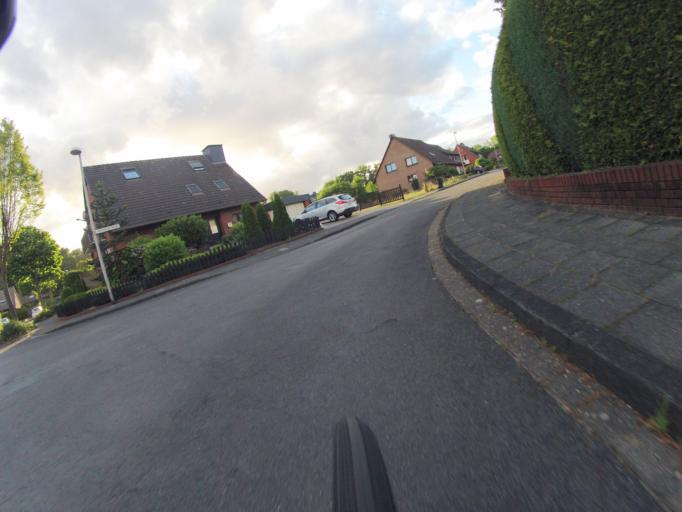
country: DE
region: North Rhine-Westphalia
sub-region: Regierungsbezirk Munster
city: Birgte
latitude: 52.2957
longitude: 7.6531
